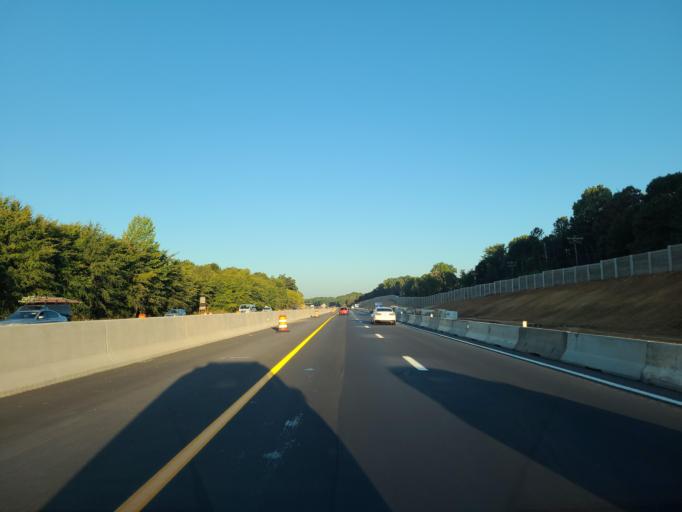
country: US
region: North Carolina
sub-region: Union County
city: Weddington
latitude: 35.0633
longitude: -80.7993
